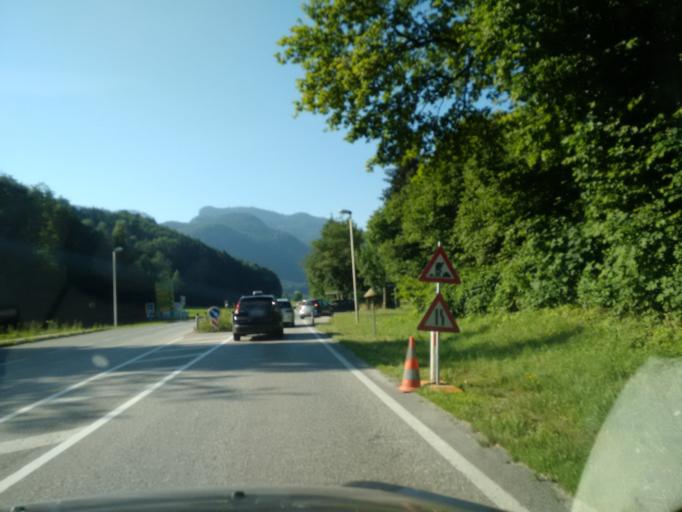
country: AT
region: Upper Austria
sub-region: Politischer Bezirk Gmunden
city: Bad Ischl
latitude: 47.6955
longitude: 13.6233
